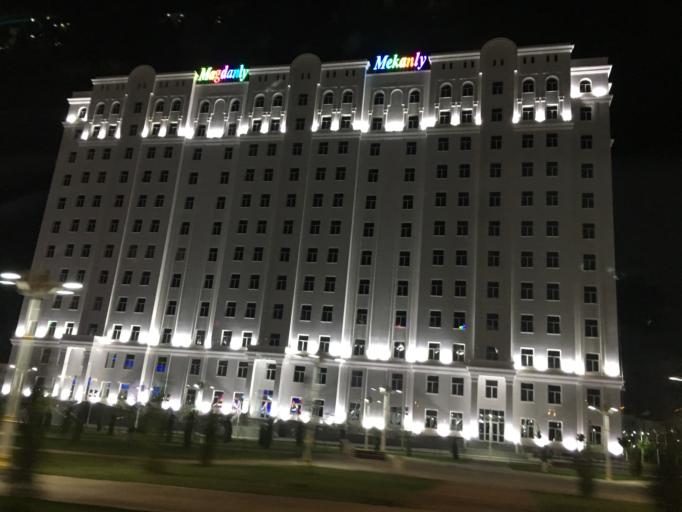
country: TM
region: Ahal
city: Ashgabat
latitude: 37.9405
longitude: 58.3514
